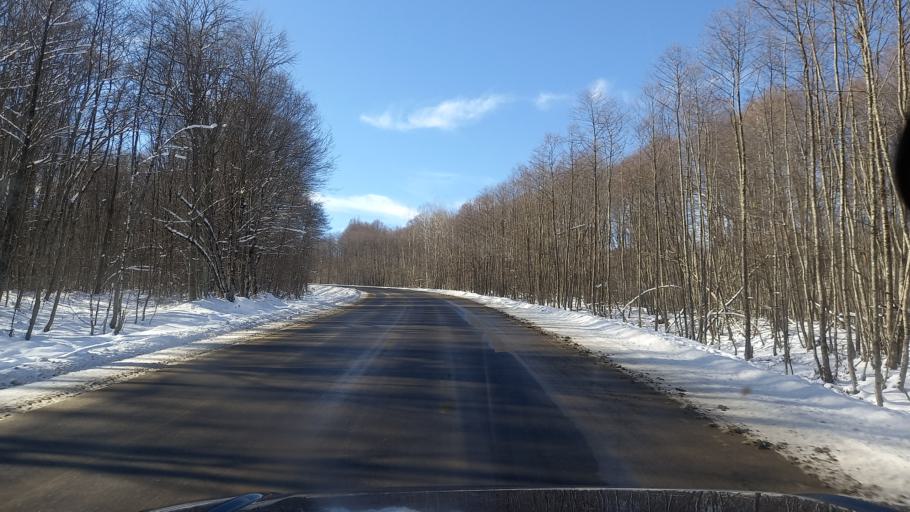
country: RU
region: Adygeya
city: Kamennomostskiy
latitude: 44.2178
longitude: 40.0808
